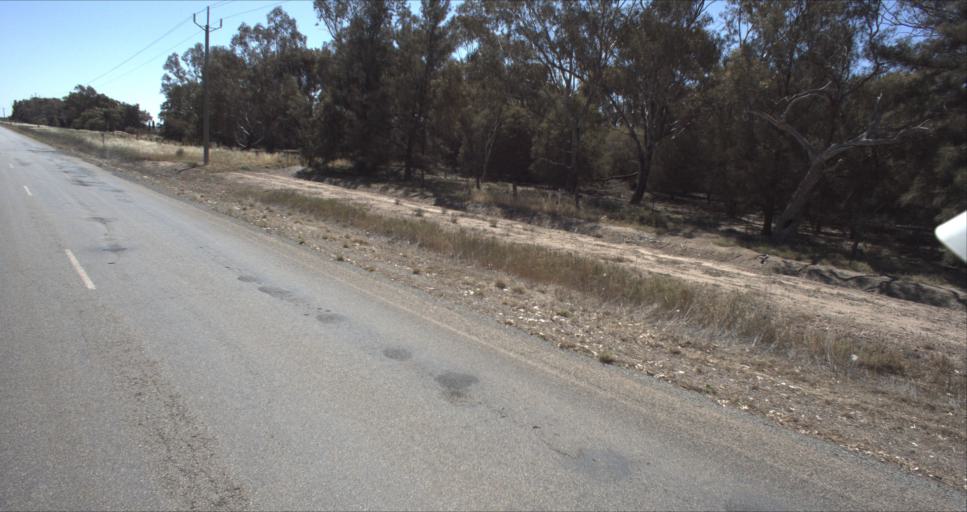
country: AU
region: New South Wales
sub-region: Leeton
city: Leeton
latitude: -34.4709
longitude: 146.2924
